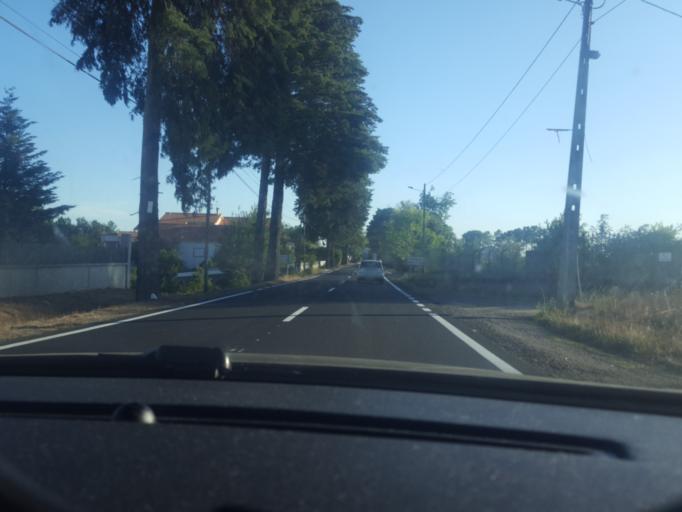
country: PT
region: Viseu
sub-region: Mangualde
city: Mangualde
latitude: 40.5826
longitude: -7.8057
